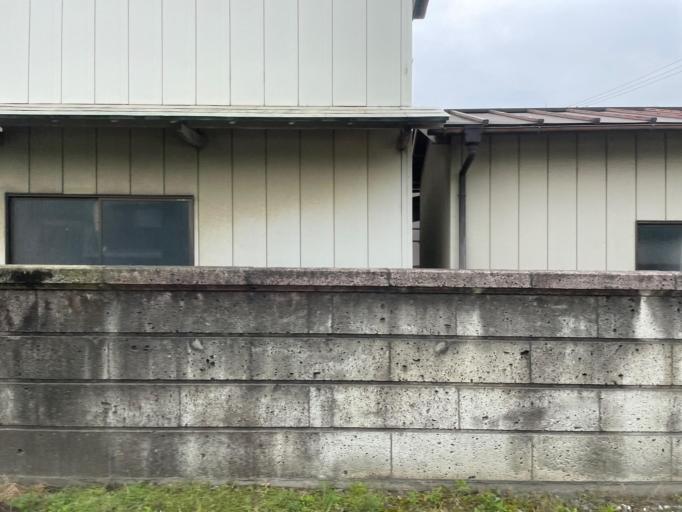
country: JP
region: Tochigi
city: Tanuma
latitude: 36.4430
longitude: 139.6506
